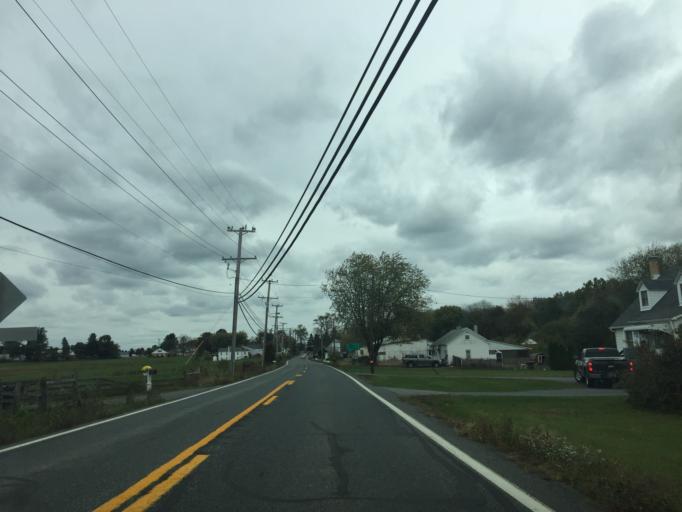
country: US
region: Maryland
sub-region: Harford County
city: Riverside
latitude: 39.5542
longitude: -76.2531
